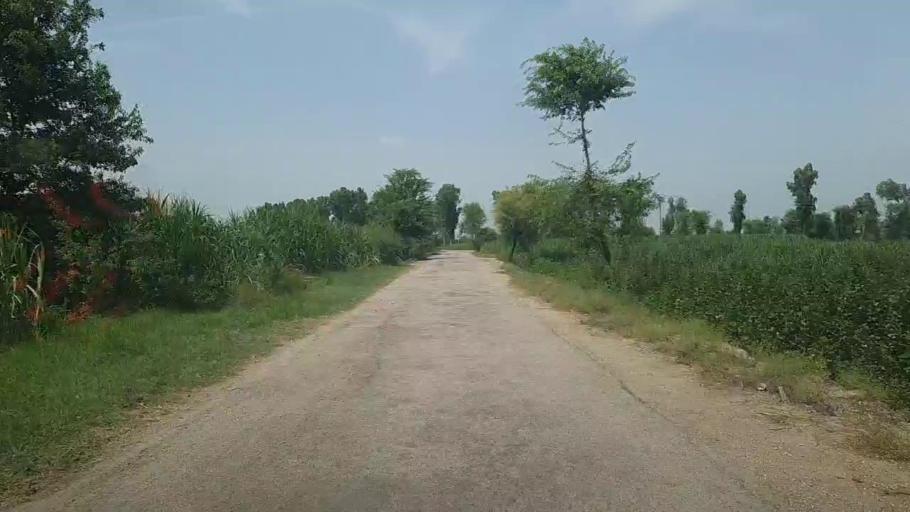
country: PK
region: Sindh
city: Ubauro
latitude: 28.1689
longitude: 69.8314
